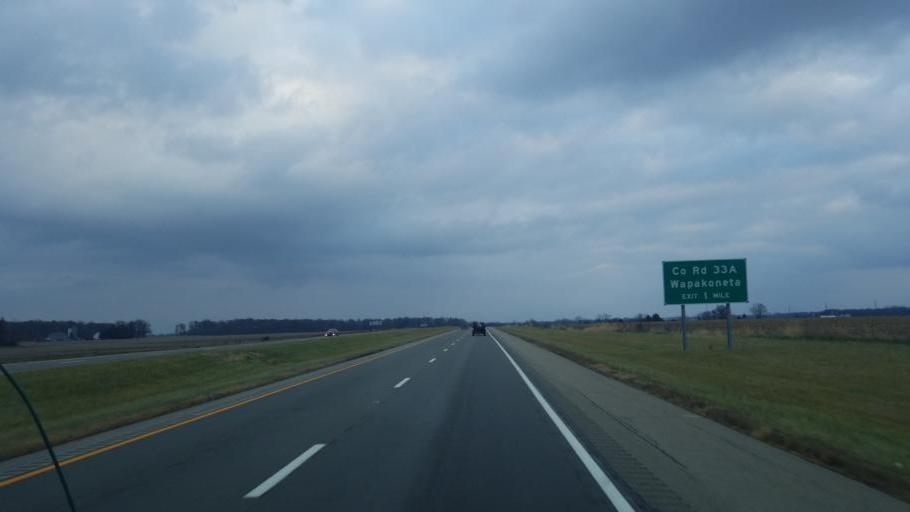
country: US
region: Ohio
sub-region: Auglaize County
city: Wapakoneta
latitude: 40.5649
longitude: -84.2544
